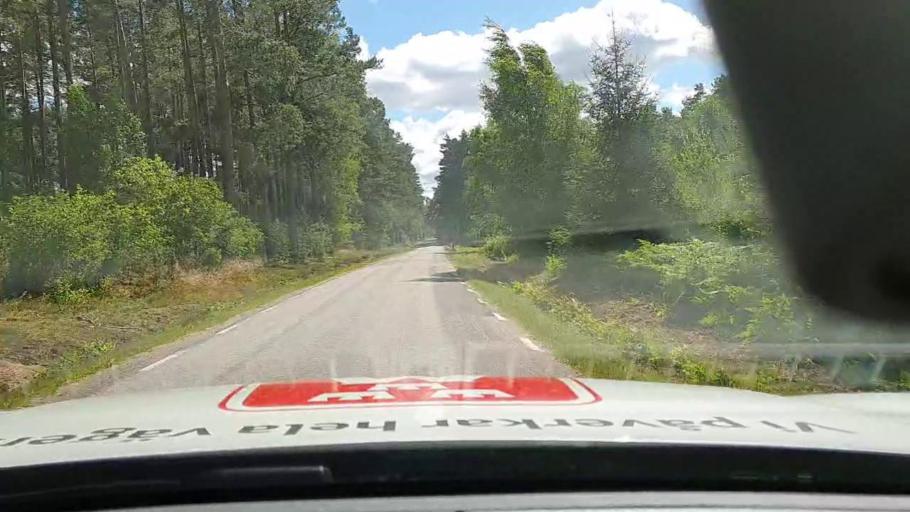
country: SE
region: Vaestra Goetaland
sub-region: Toreboda Kommun
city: Toereboda
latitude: 58.5789
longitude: 14.1237
